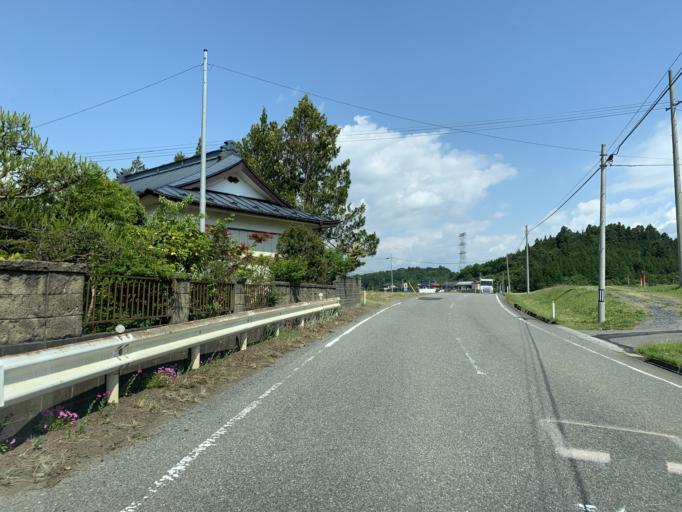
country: JP
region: Iwate
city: Ichinoseki
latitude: 38.7985
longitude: 141.0169
